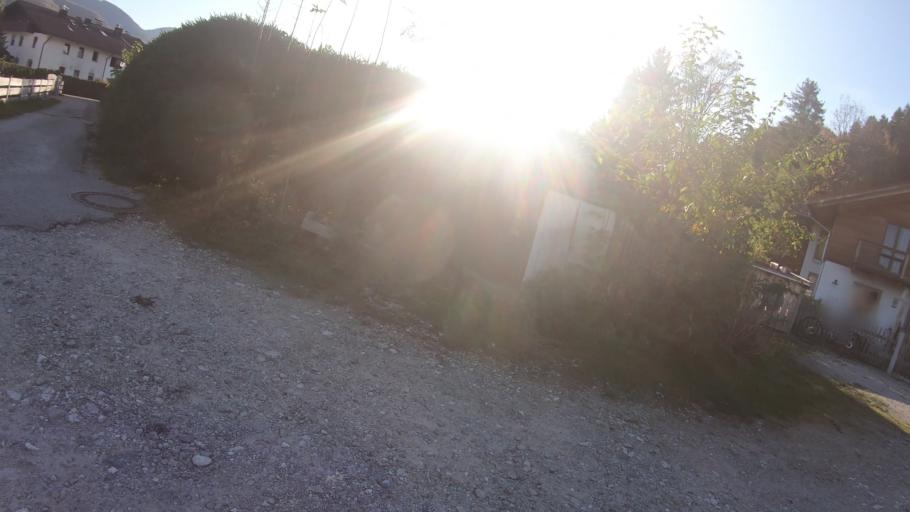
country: DE
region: Bavaria
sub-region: Upper Bavaria
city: Bergen
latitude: 47.8102
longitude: 12.5871
